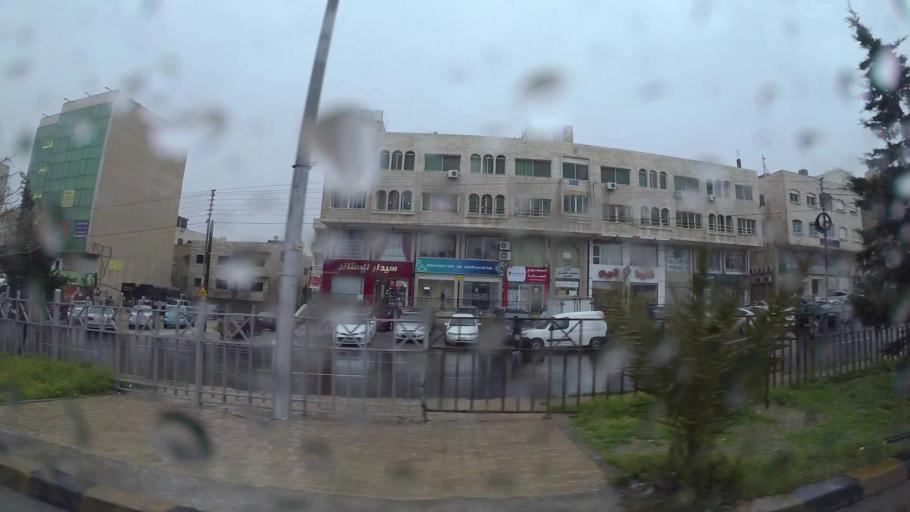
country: JO
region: Amman
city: Al Jubayhah
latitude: 32.0517
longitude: 35.8802
